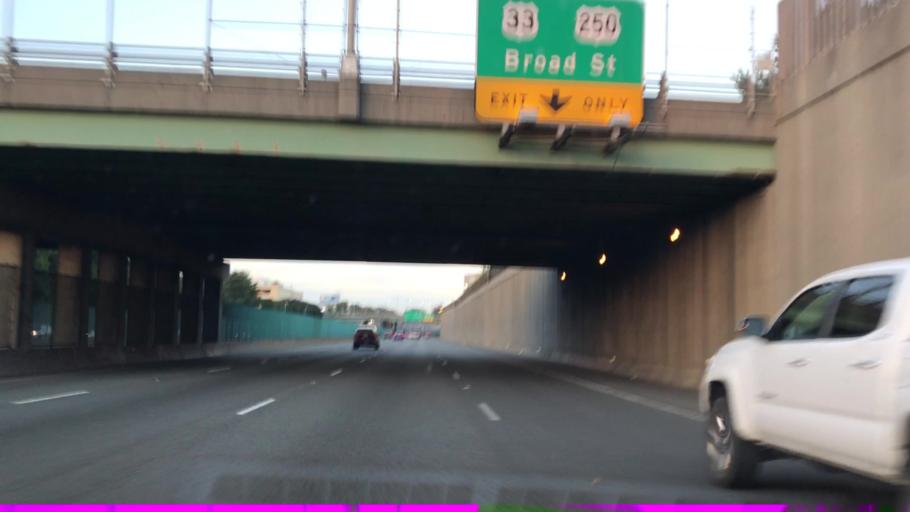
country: US
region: Virginia
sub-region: City of Richmond
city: Richmond
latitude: 37.5663
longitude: -77.4816
